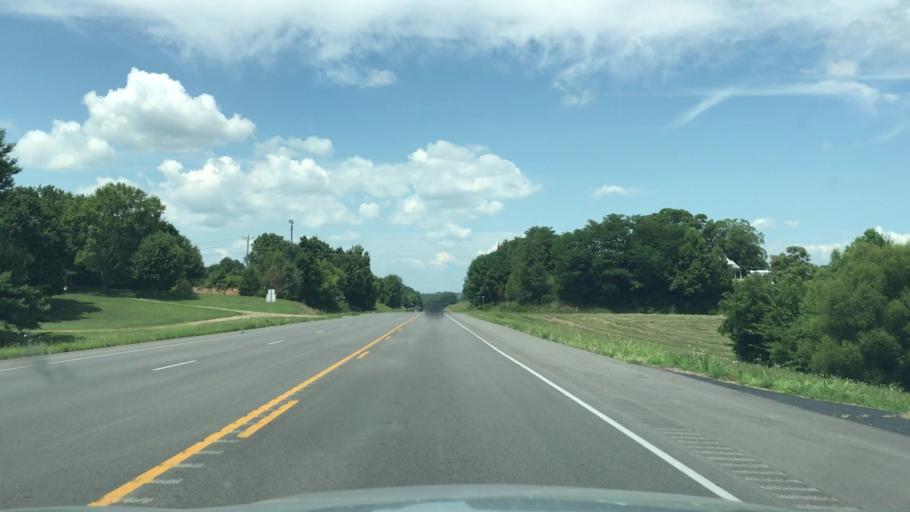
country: US
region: Kentucky
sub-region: Clinton County
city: Albany
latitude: 36.7542
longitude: -85.0990
